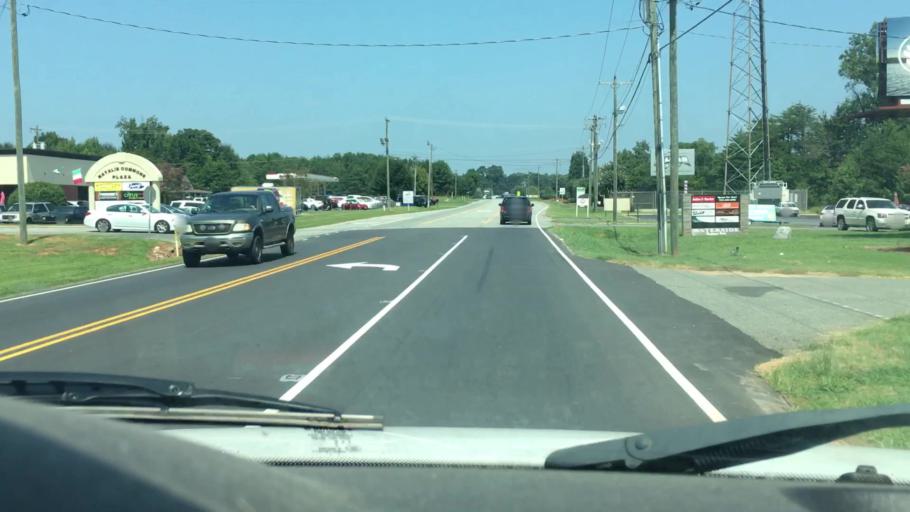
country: US
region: North Carolina
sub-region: Lincoln County
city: Westport
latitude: 35.4824
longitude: -80.9939
